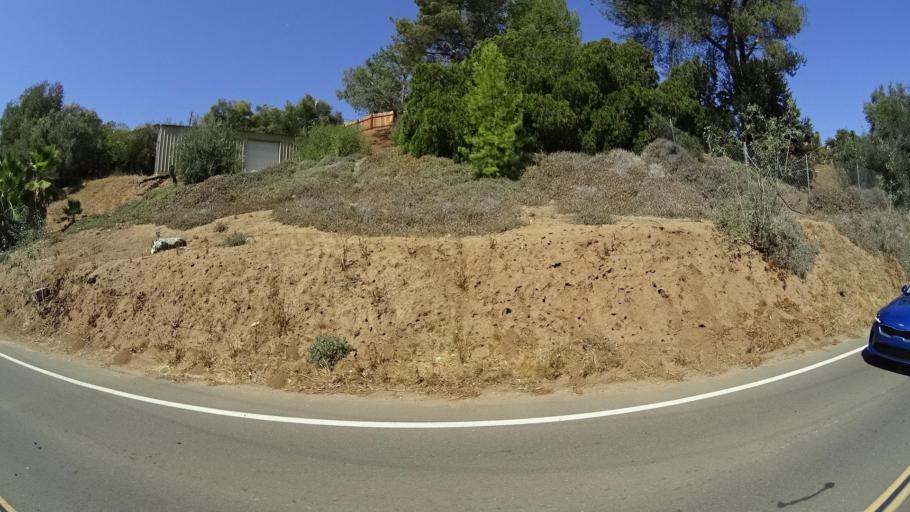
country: US
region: California
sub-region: San Diego County
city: Lakeside
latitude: 32.8533
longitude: -116.9215
